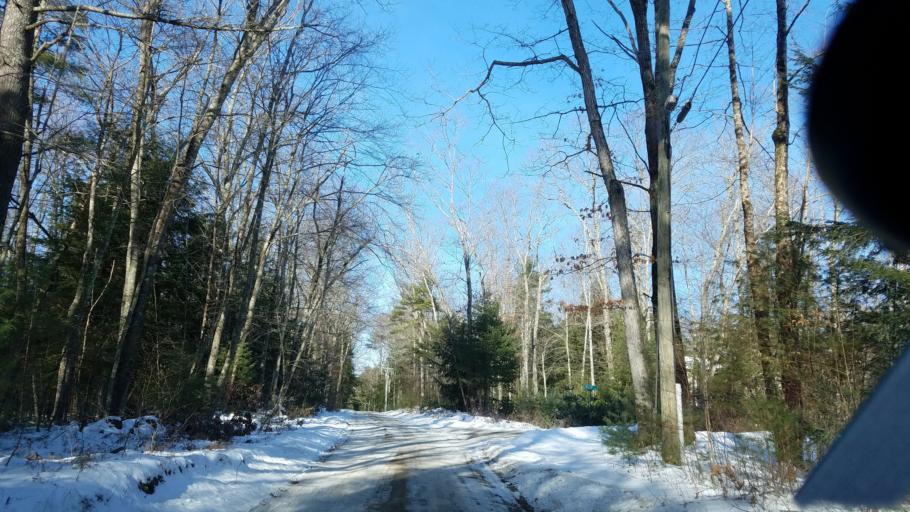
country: US
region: Massachusetts
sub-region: Hampden County
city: Holland
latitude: 41.9652
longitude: -72.0978
